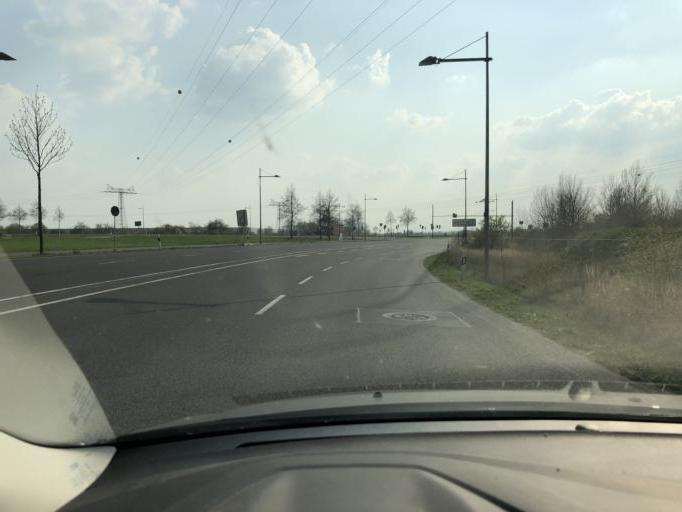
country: DE
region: Saxony
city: Taucha
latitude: 51.4013
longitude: 12.4318
